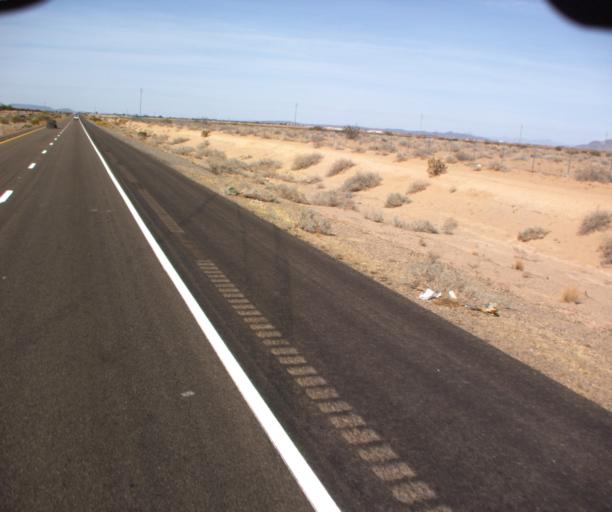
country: US
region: Arizona
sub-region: Yuma County
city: Fortuna Foothills
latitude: 32.6386
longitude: -114.5213
